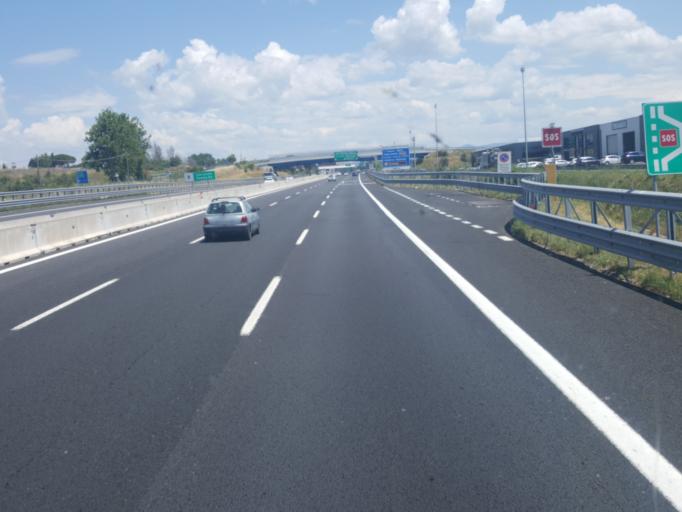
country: IT
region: Latium
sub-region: Citta metropolitana di Roma Capitale
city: Bivio di Capanelle
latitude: 42.1264
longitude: 12.5975
